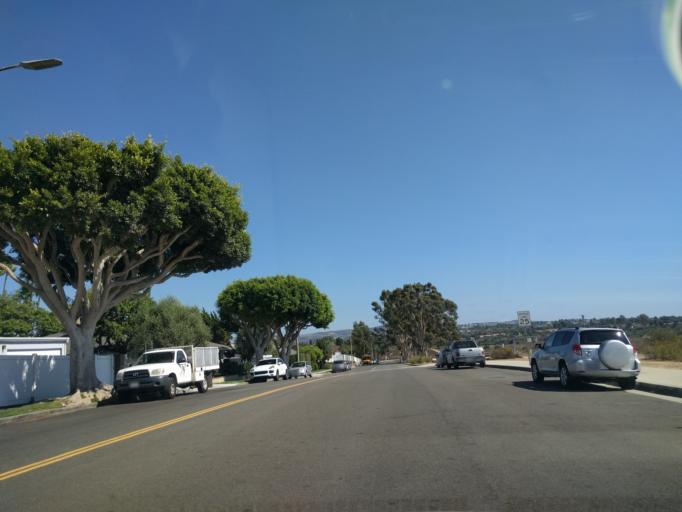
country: US
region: California
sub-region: Orange County
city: Costa Mesa
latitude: 33.6554
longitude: -117.8864
